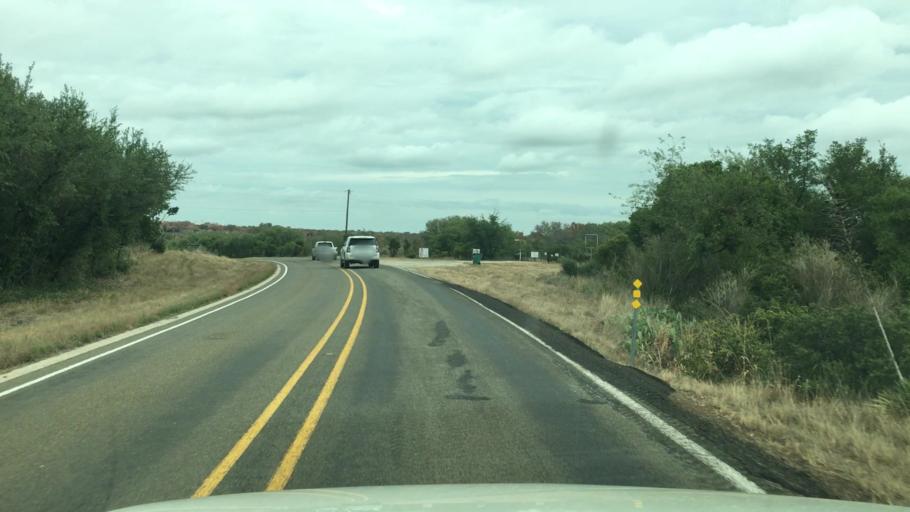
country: US
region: Texas
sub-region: Llano County
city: Horseshoe Bay
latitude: 30.4776
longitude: -98.4175
